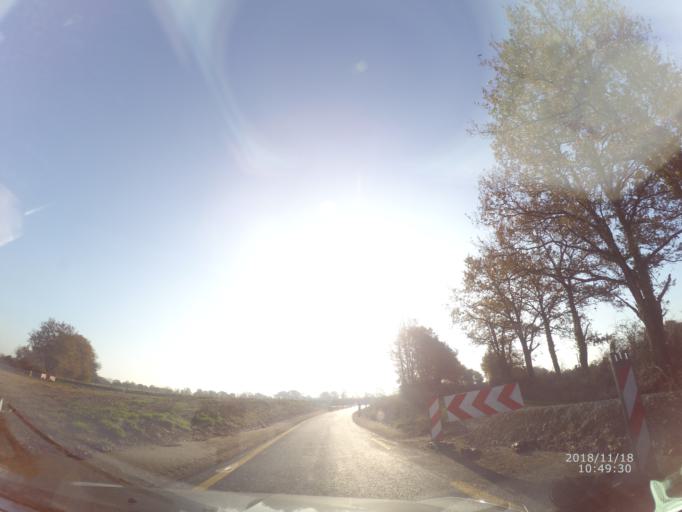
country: FR
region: Pays de la Loire
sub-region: Departement de la Loire-Atlantique
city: Vue
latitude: 47.2045
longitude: -1.9196
